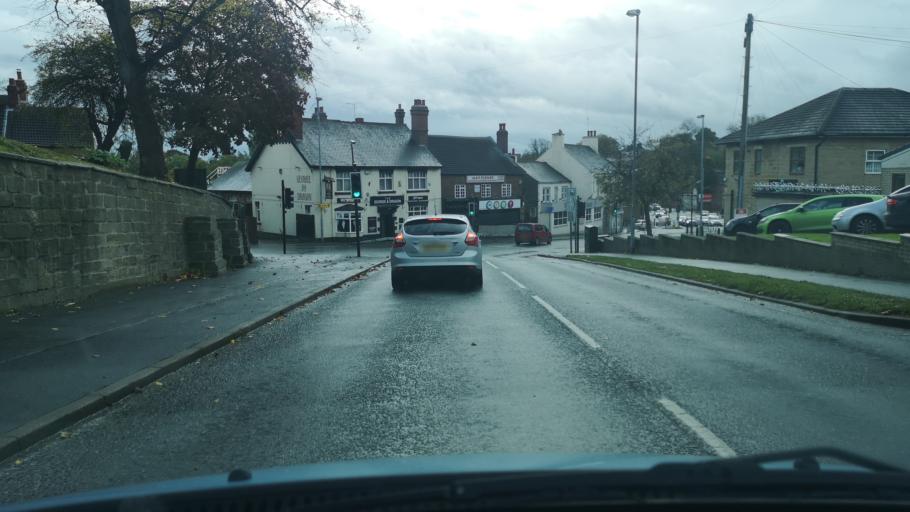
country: GB
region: England
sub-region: City and Borough of Wakefield
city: Hemsworth
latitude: 53.6142
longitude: -1.3536
